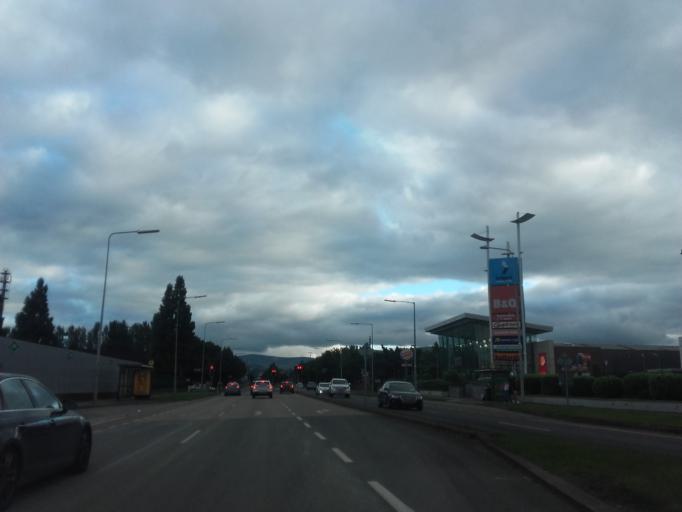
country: IE
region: Leinster
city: Tallaght
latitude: 53.2940
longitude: -6.3692
